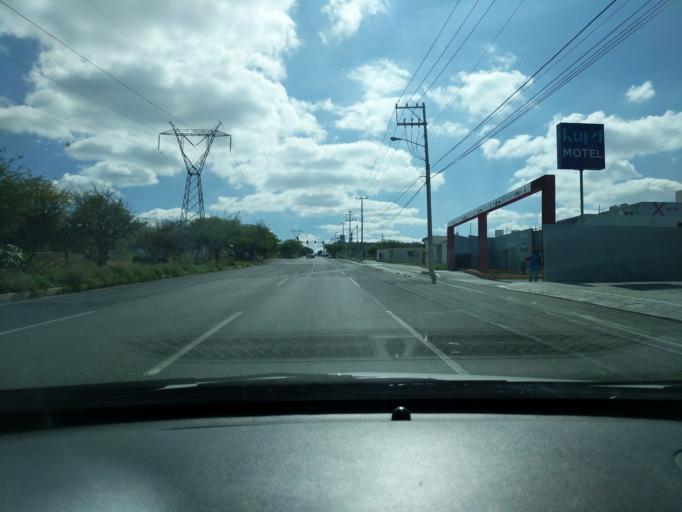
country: MX
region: Queretaro
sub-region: Queretaro
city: Patria Nueva
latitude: 20.6412
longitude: -100.4936
